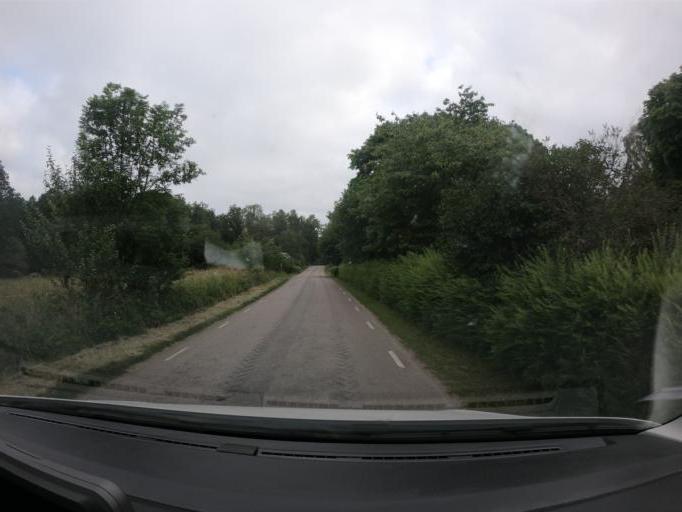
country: SE
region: Skane
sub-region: Klippans Kommun
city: Ljungbyhed
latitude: 56.0504
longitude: 13.2551
